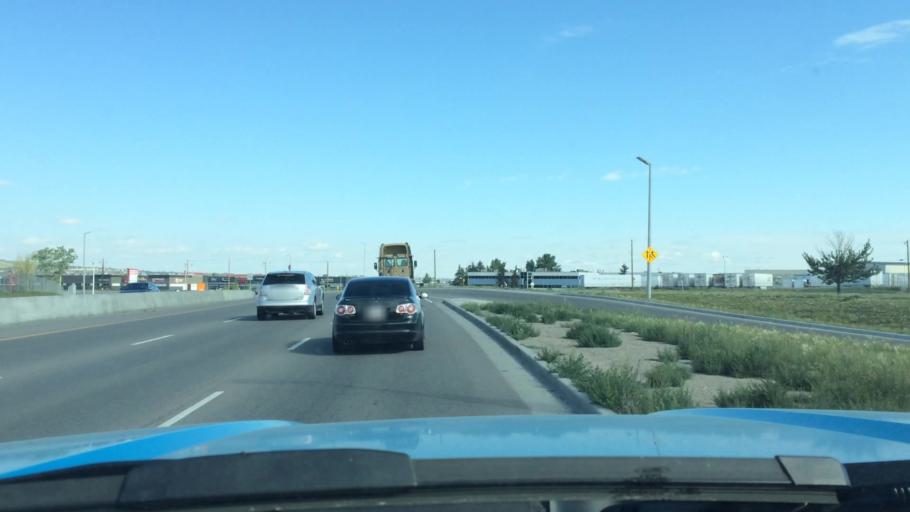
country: CA
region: Alberta
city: Calgary
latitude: 51.0950
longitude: -114.0264
